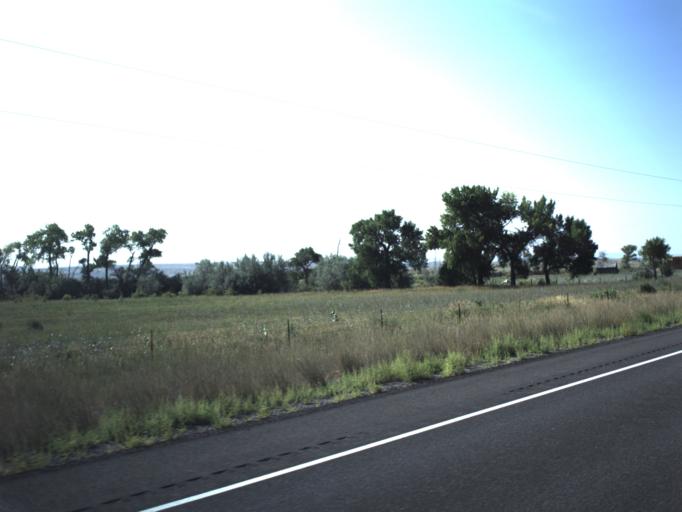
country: US
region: Utah
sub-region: Emery County
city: Huntington
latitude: 39.2655
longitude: -110.9809
